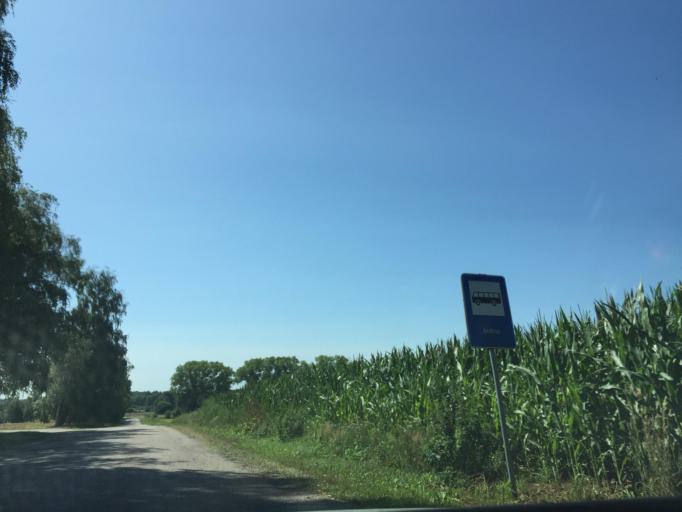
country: LV
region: Talsu Rajons
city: Stende
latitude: 57.1415
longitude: 22.6605
